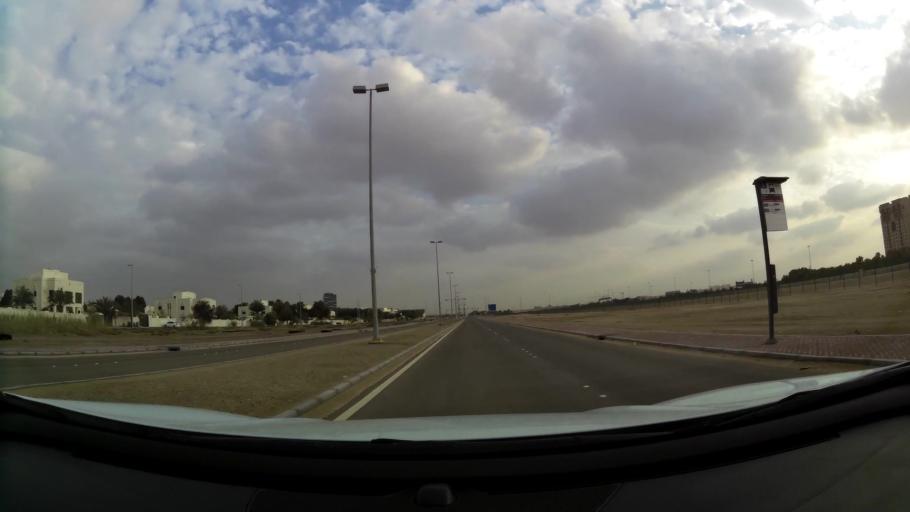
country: AE
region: Abu Dhabi
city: Abu Dhabi
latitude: 24.3863
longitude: 54.5270
